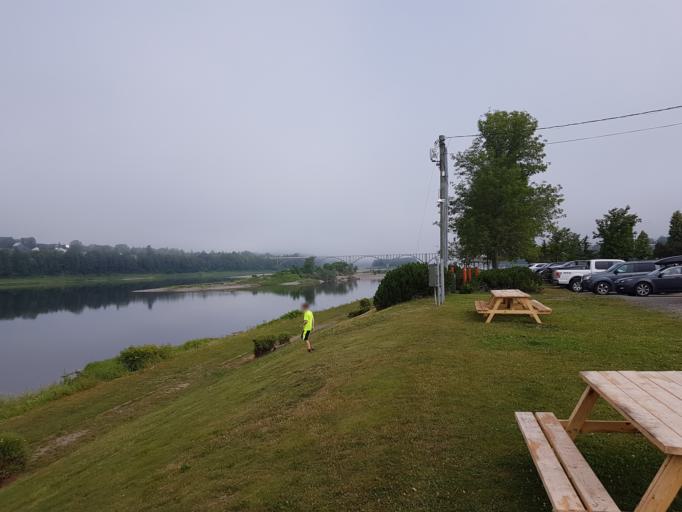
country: CA
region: New Brunswick
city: Florenceville-Bristol
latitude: 46.2974
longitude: -67.5283
